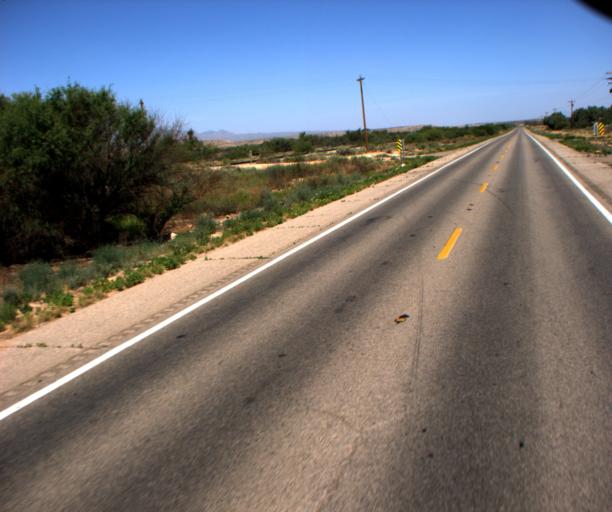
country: US
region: Arizona
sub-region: Graham County
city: Bylas
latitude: 33.0528
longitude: -109.9936
